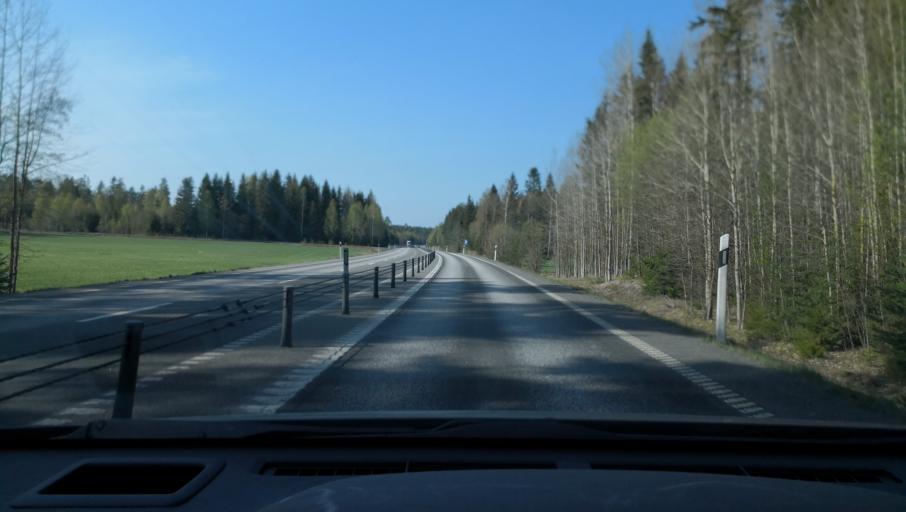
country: SE
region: Uppsala
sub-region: Heby Kommun
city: Tarnsjo
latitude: 60.1741
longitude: 16.9528
